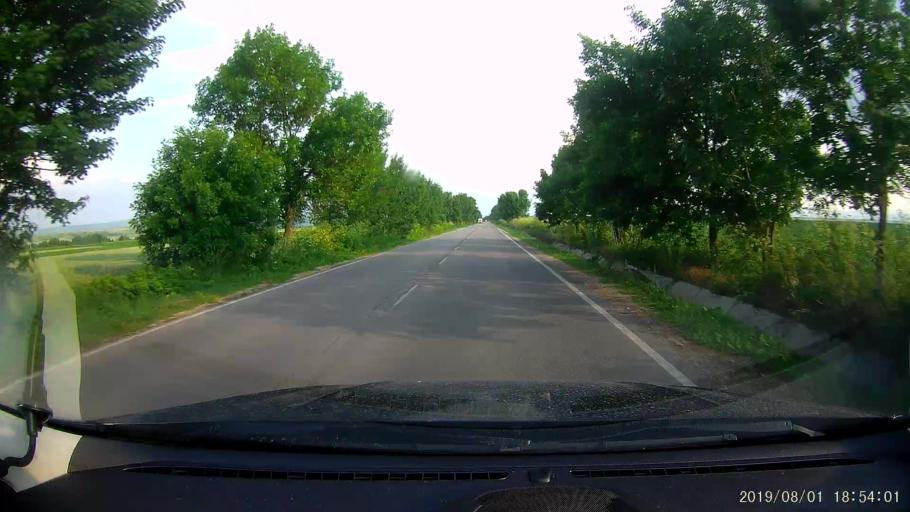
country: BG
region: Shumen
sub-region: Obshtina Shumen
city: Shumen
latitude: 43.2089
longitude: 26.9990
